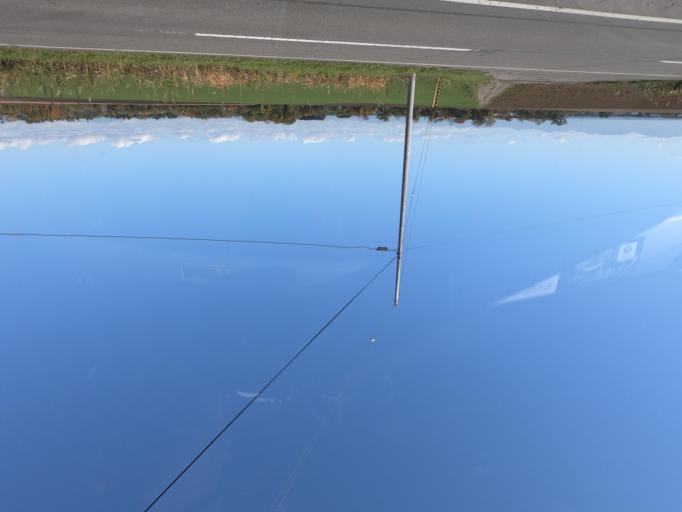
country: JP
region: Hokkaido
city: Otofuke
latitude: 43.0374
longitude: 143.2719
